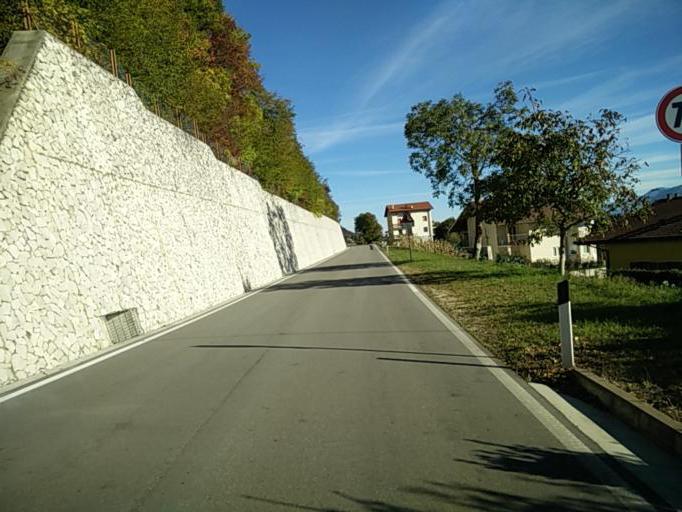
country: IT
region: Trentino-Alto Adige
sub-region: Provincia di Trento
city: Garniga Nuova
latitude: 45.9906
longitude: 11.0835
